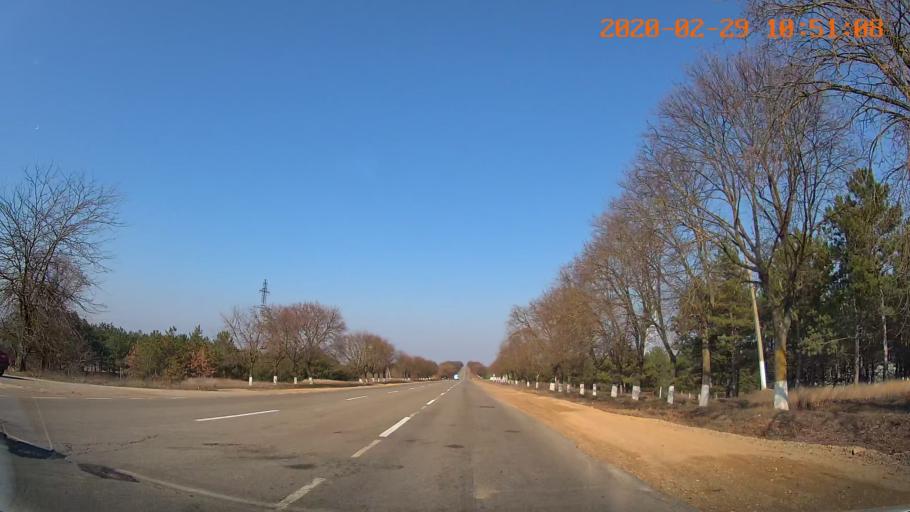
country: MD
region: Telenesti
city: Grigoriopol
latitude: 47.0900
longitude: 29.3682
